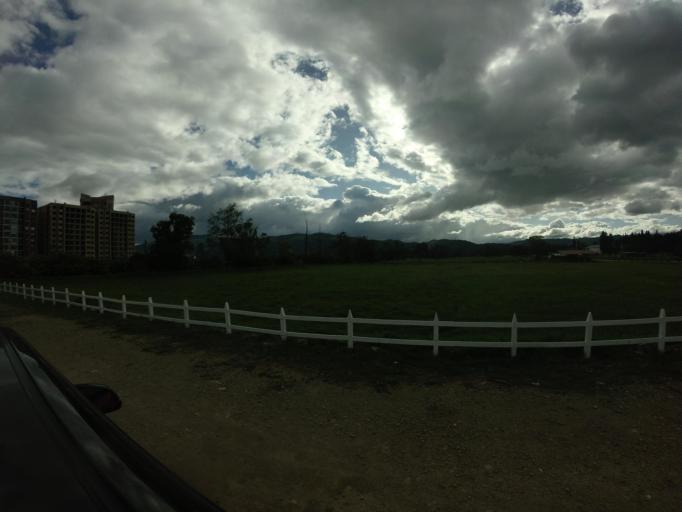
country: CO
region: Cundinamarca
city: Sopo
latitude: 4.9128
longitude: -73.9434
